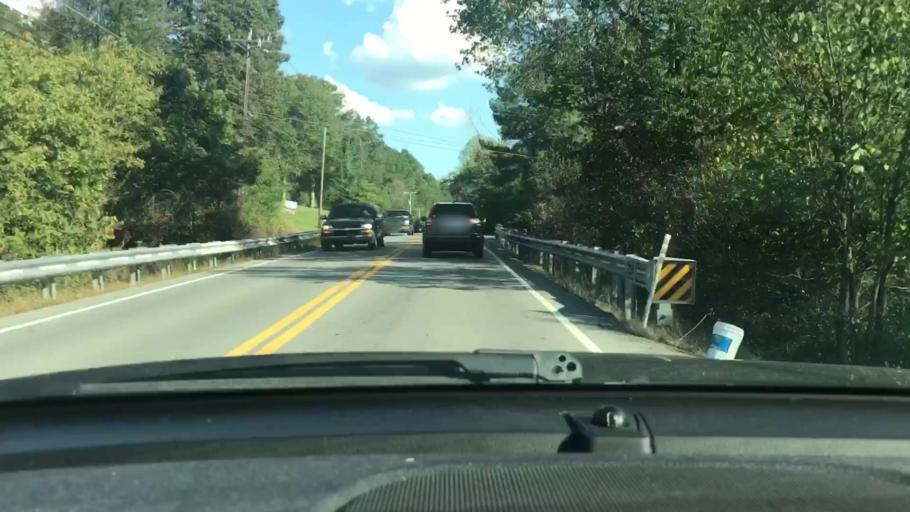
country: US
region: Tennessee
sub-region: Sumner County
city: Shackle Island
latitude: 36.4140
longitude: -86.6453
